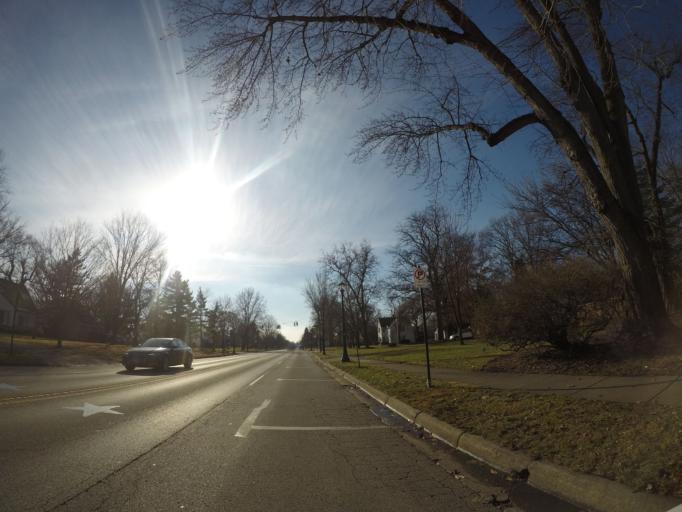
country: US
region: Ohio
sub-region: Franklin County
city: Upper Arlington
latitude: 40.0124
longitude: -83.0579
